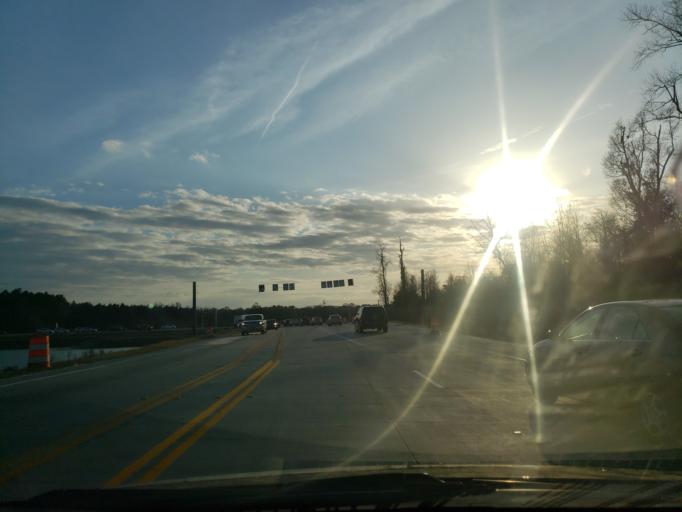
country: US
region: Georgia
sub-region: Chatham County
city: Bloomingdale
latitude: 32.1378
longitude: -81.3101
